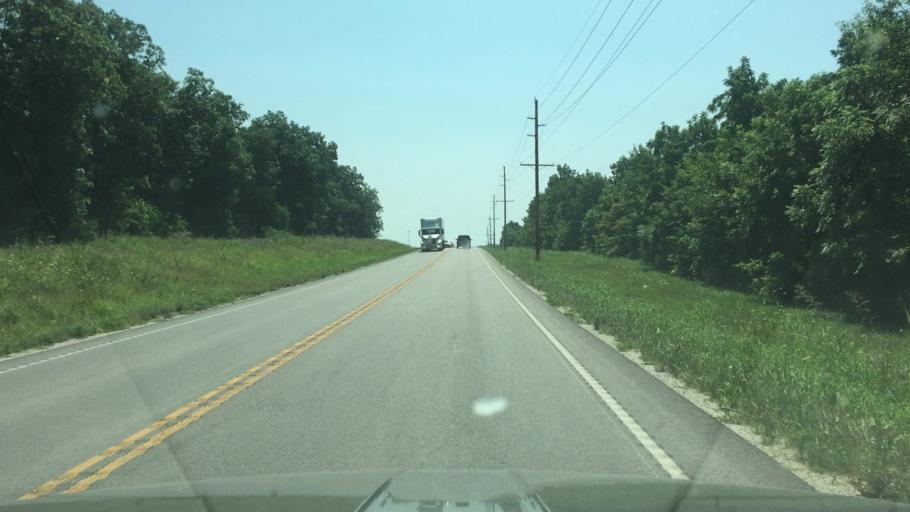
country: US
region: Missouri
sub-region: Miller County
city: Eldon
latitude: 38.3876
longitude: -92.6960
